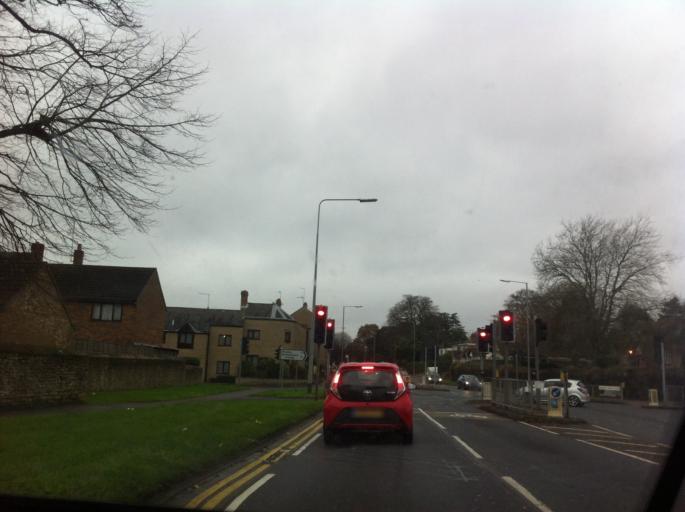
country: GB
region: England
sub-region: Northamptonshire
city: Earls Barton
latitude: 52.2649
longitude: -0.7407
